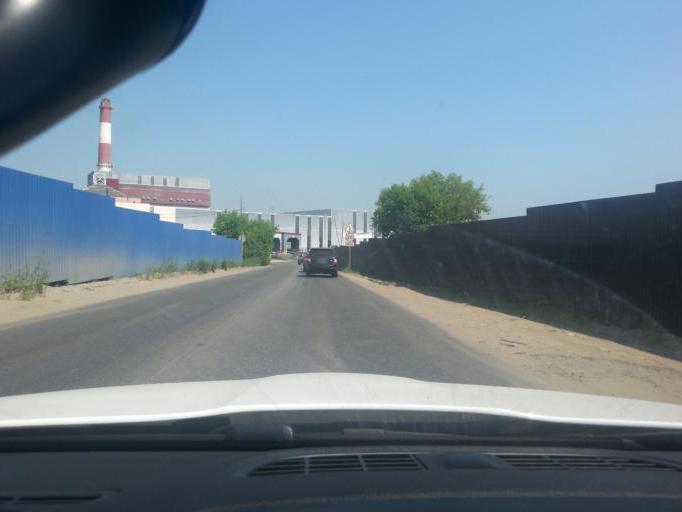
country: RU
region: Moscow
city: Nekrasovka
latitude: 55.7155
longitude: 37.9338
